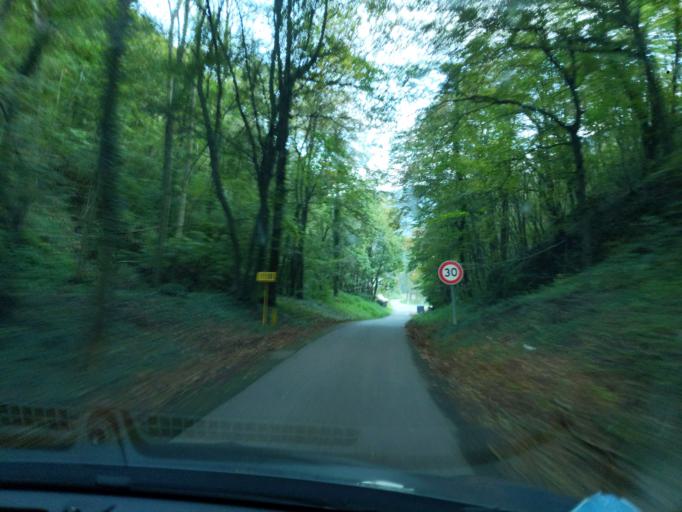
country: FR
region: Rhone-Alpes
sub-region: Departement de la Savoie
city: Aiton
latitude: 45.5337
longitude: 6.3081
